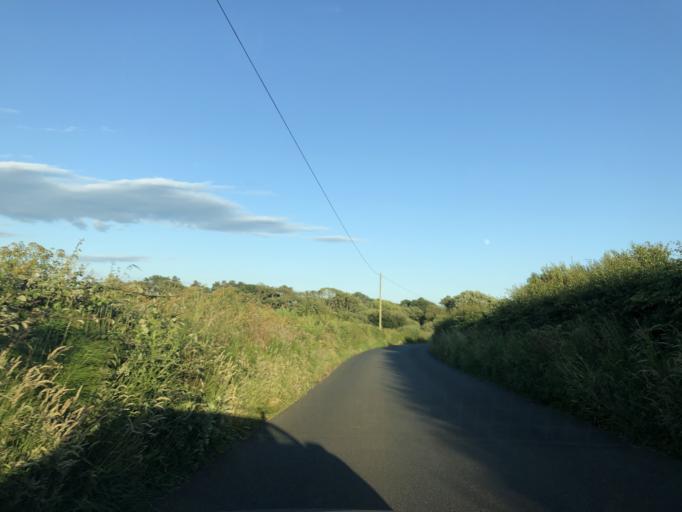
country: GB
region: England
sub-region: Isle of Wight
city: Chale
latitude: 50.6331
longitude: -1.3266
